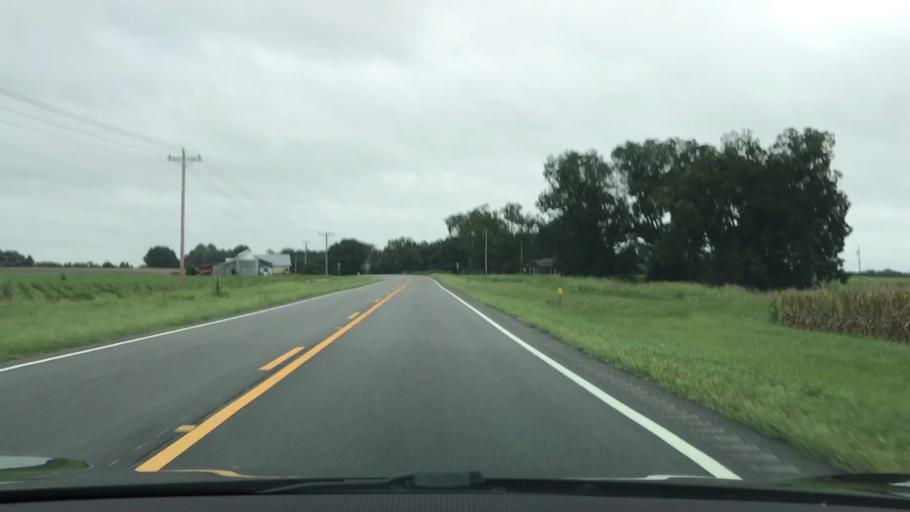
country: US
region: Alabama
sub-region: Covington County
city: Opp
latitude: 31.2718
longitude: -86.1595
